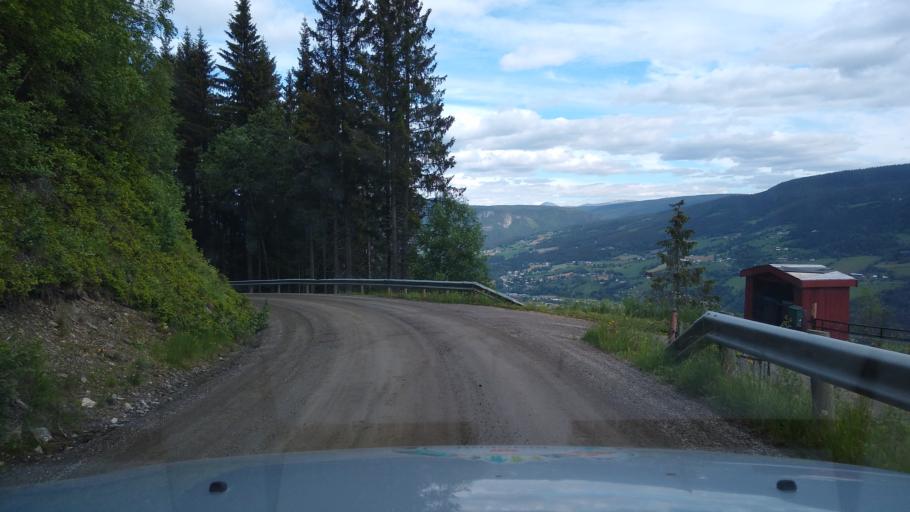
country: NO
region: Oppland
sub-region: Ringebu
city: Ringebu
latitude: 61.5005
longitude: 10.1406
